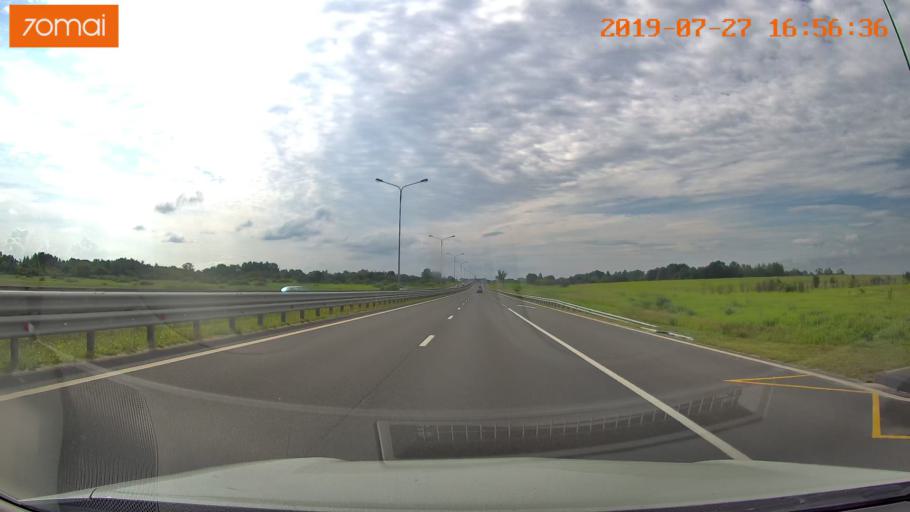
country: RU
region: Kaliningrad
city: Bol'shoe Isakovo
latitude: 54.6957
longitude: 20.7344
